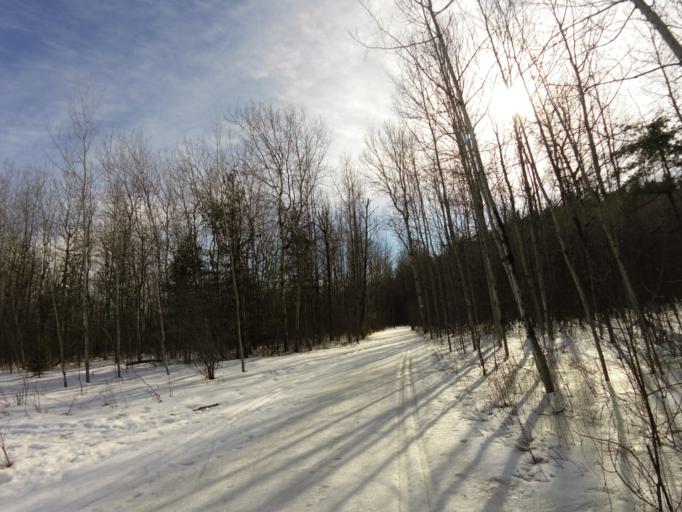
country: CA
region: Quebec
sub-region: Outaouais
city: Gatineau
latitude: 45.4577
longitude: -75.7725
